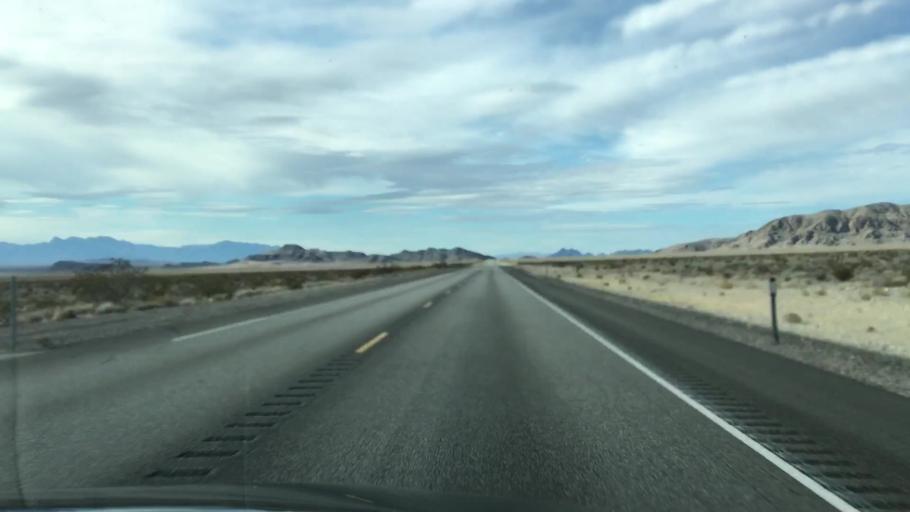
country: US
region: Nevada
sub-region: Nye County
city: Pahrump
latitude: 36.5698
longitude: -116.1574
